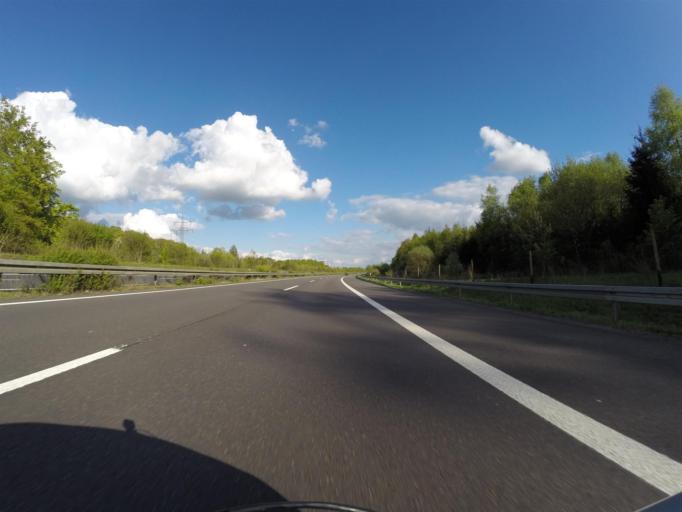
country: DE
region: Saarland
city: Orscholz
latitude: 49.4659
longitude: 6.4670
